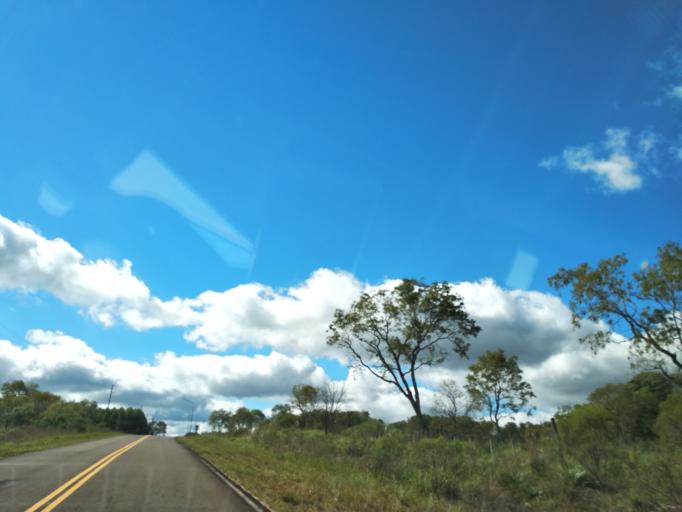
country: AR
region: Misiones
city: Santa Ana
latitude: -27.4095
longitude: -55.5552
